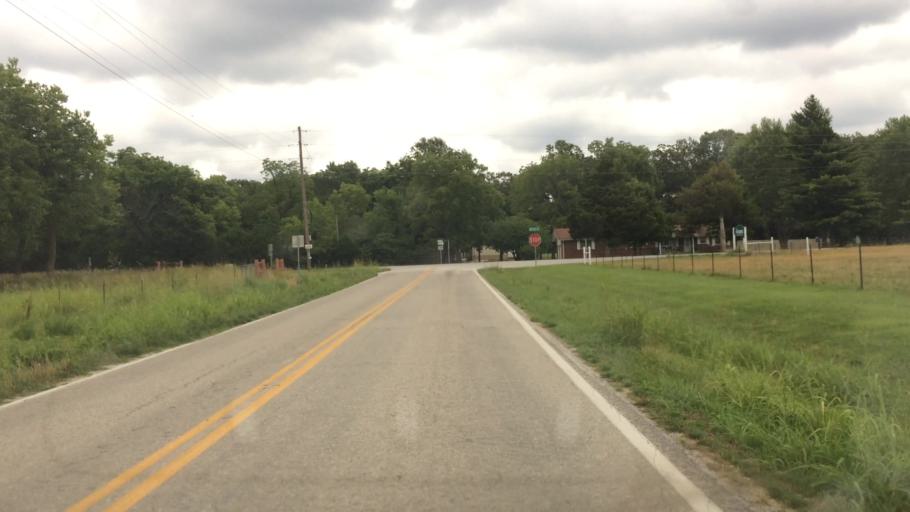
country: US
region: Missouri
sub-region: Greene County
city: Strafford
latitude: 37.2959
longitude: -93.1139
